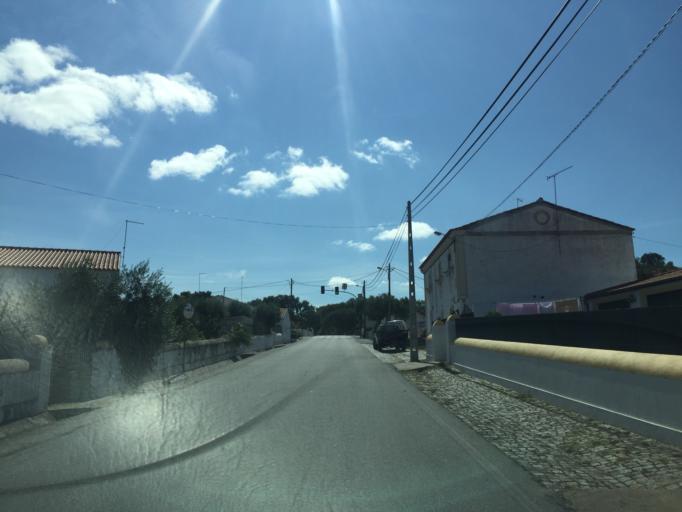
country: PT
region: Portalegre
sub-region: Marvao
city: Marvao
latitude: 39.4345
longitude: -7.3635
